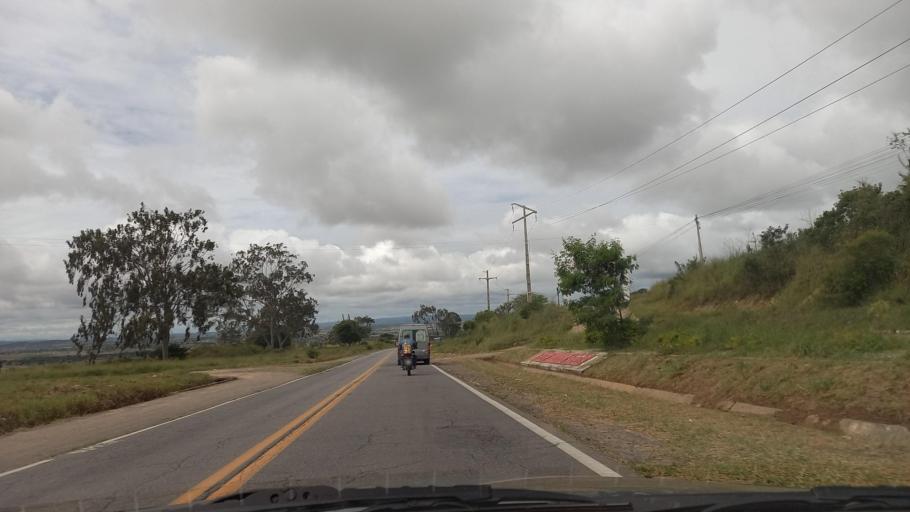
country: BR
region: Pernambuco
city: Garanhuns
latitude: -8.8774
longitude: -36.4499
